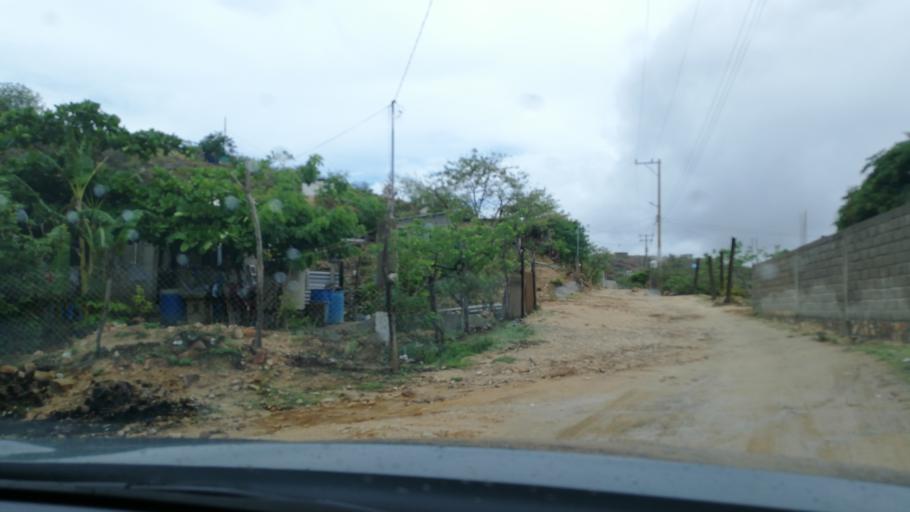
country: MX
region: Oaxaca
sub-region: Salina Cruz
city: Salina Cruz
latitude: 16.1806
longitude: -95.1813
